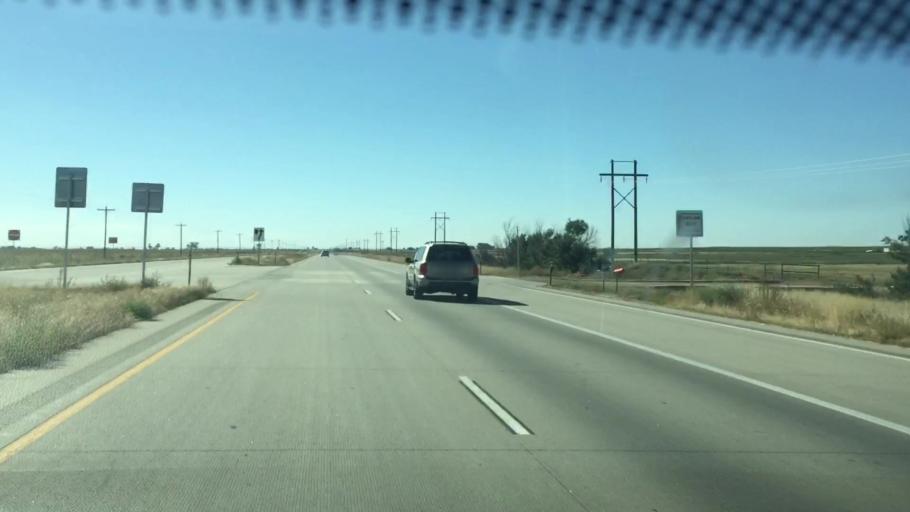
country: US
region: Colorado
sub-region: Prowers County
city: Lamar
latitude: 38.1113
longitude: -102.6609
